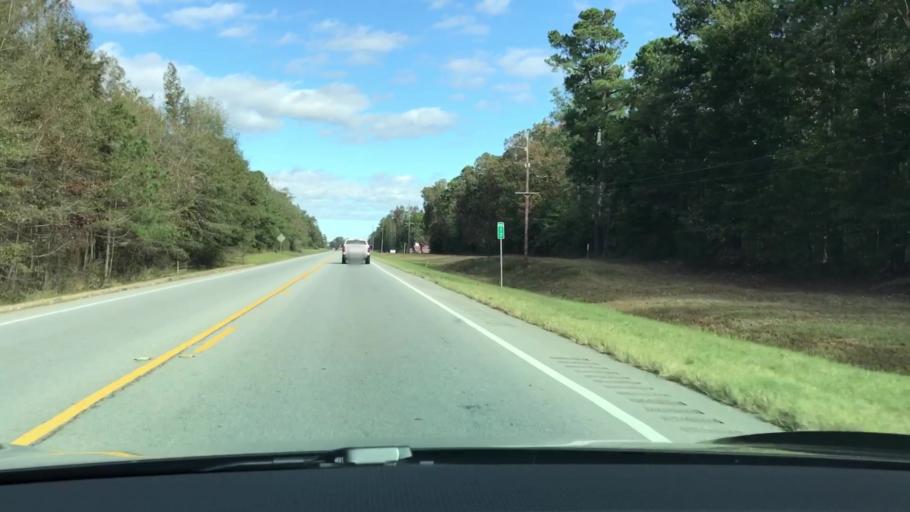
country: US
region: Georgia
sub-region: Jefferson County
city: Louisville
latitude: 33.0570
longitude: -82.4058
